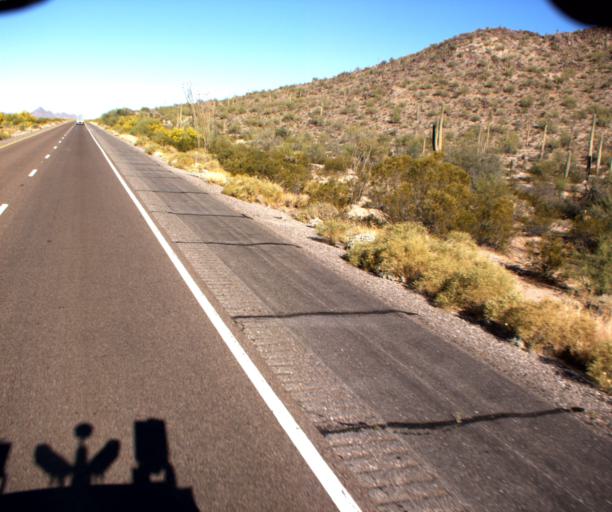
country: US
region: Arizona
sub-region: Maricopa County
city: Gila Bend
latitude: 32.8626
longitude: -112.4030
